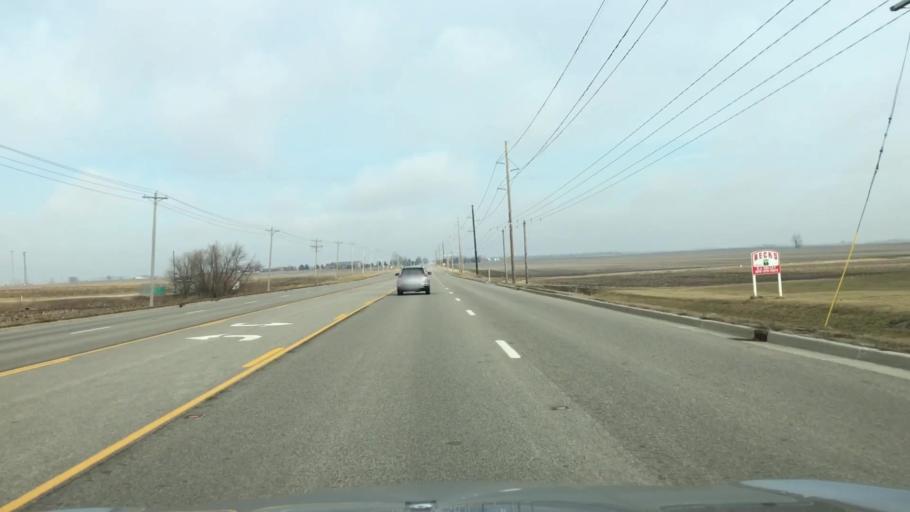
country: US
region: Illinois
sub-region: McLean County
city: Normal
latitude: 40.5209
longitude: -88.9029
